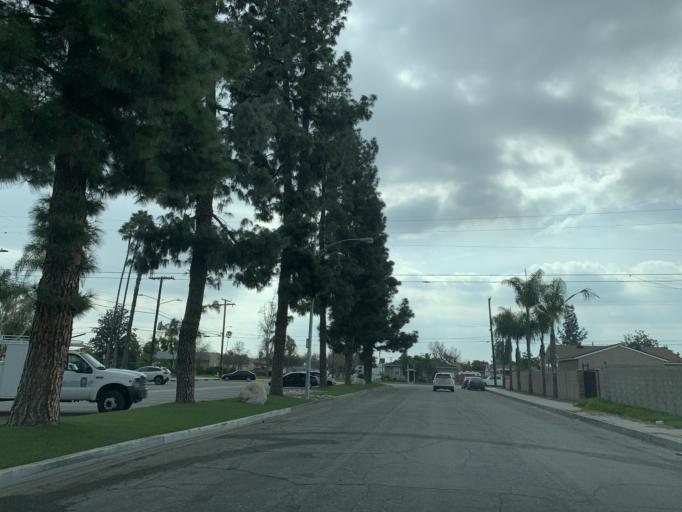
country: US
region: California
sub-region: Los Angeles County
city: Azusa
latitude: 34.1270
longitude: -117.9138
